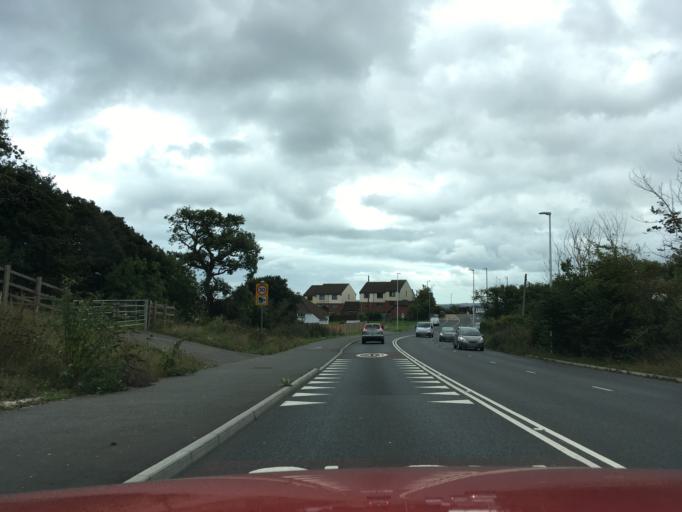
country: GB
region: England
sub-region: Devon
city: Marldon
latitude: 50.4467
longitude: -3.5908
